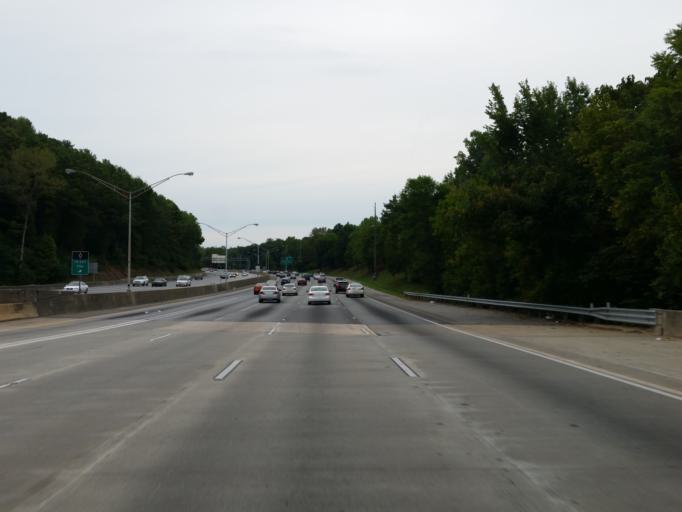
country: US
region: Georgia
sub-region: Cobb County
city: Vinings
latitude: 33.8535
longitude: -84.4313
